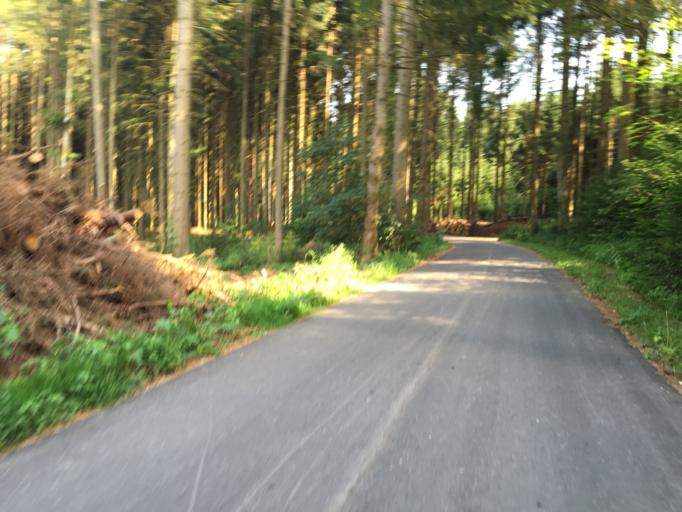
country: CH
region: Bern
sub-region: Bern-Mittelland District
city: Muri
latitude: 46.9246
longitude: 7.5190
